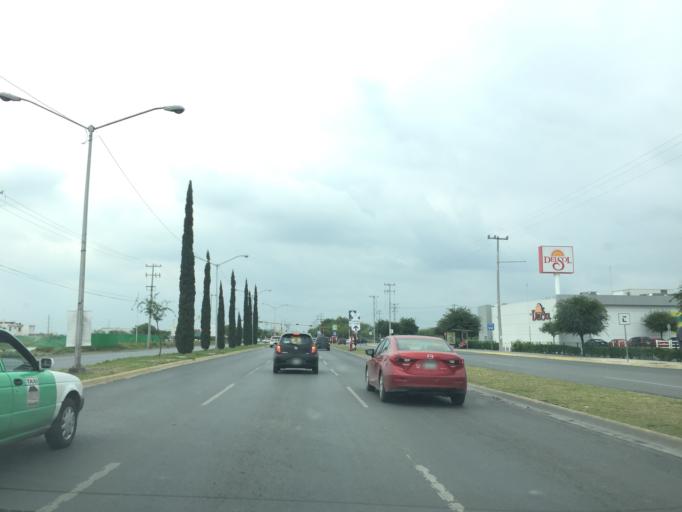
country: MX
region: Nuevo Leon
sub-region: Apodaca
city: Fraccionamiento Cosmopolis Octavo Sector
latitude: 25.7841
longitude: -100.2347
